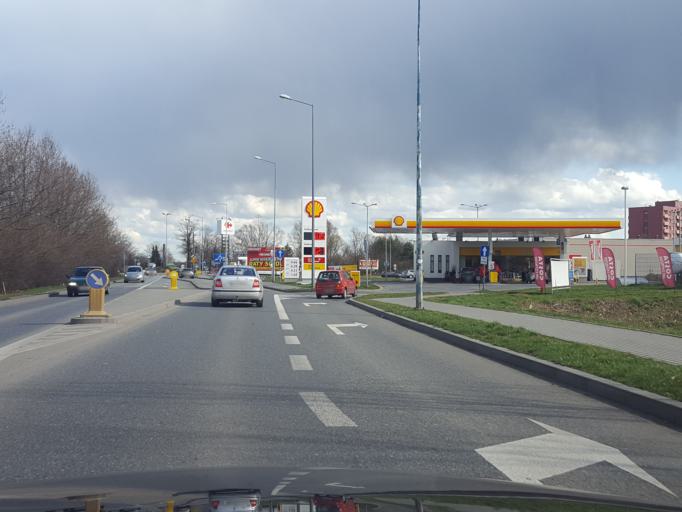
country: PL
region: Silesian Voivodeship
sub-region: Powiat pszczynski
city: Pszczyna
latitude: 49.9705
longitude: 18.9443
